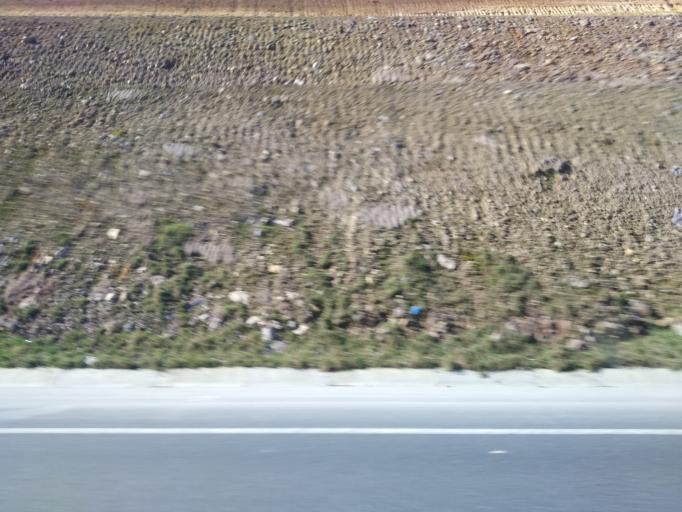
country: TR
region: Istanbul
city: Sancaktepe
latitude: 41.0954
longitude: 29.2877
